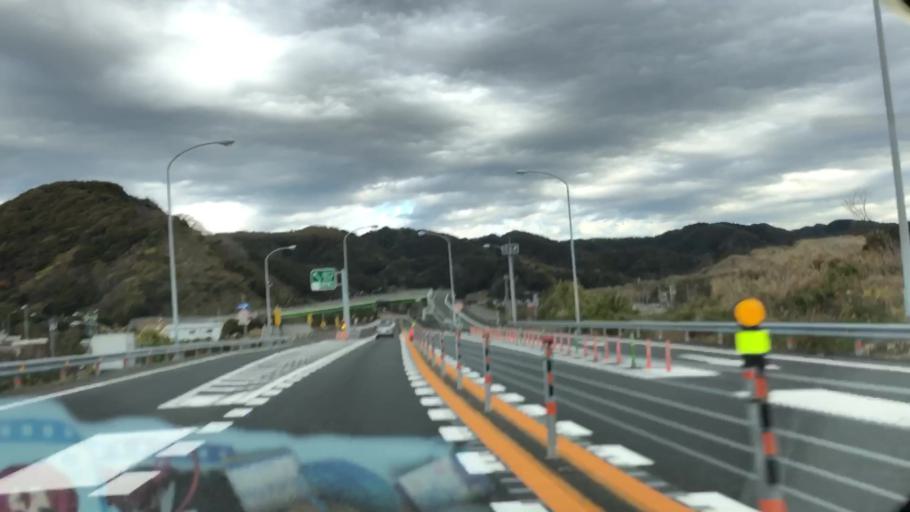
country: JP
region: Chiba
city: Tateyama
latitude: 35.1121
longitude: 139.8508
